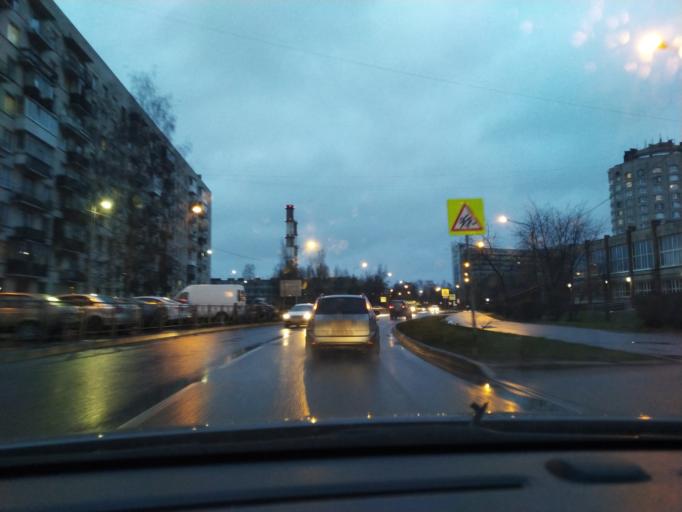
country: RU
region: St.-Petersburg
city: Uritsk
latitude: 59.8339
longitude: 30.1823
